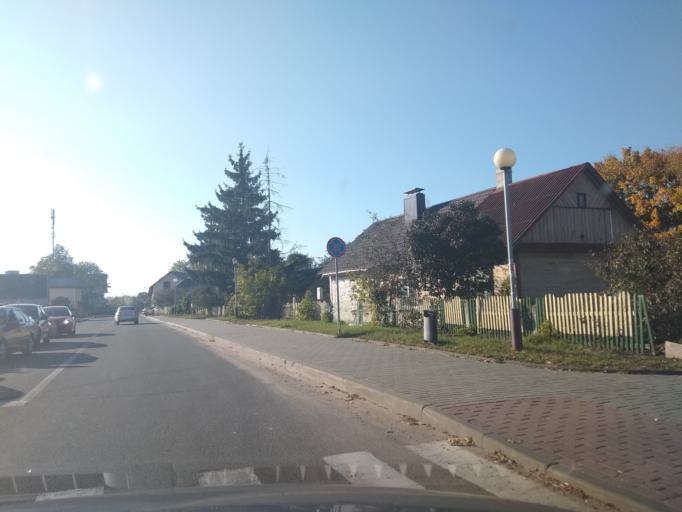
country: BY
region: Grodnenskaya
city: Vawkavysk
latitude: 53.1577
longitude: 24.4543
